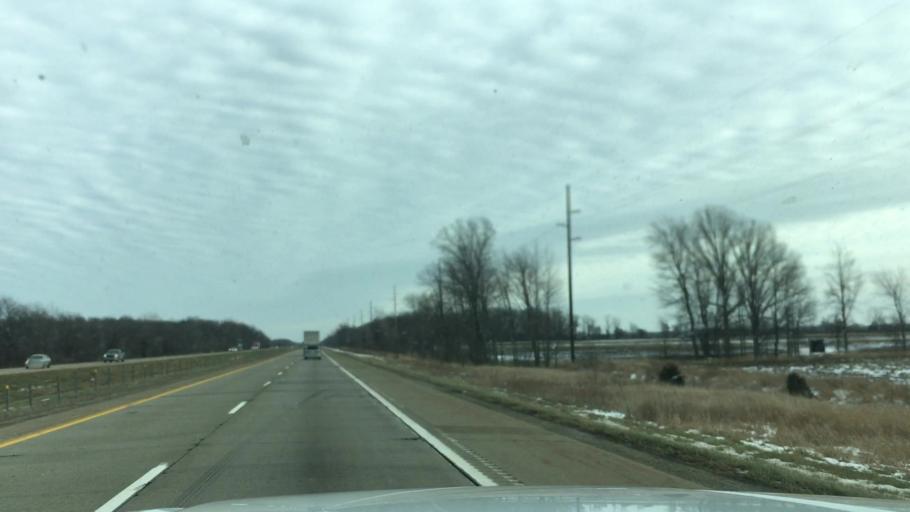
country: US
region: Michigan
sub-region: Ionia County
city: Portland
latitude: 42.8787
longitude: -85.0154
